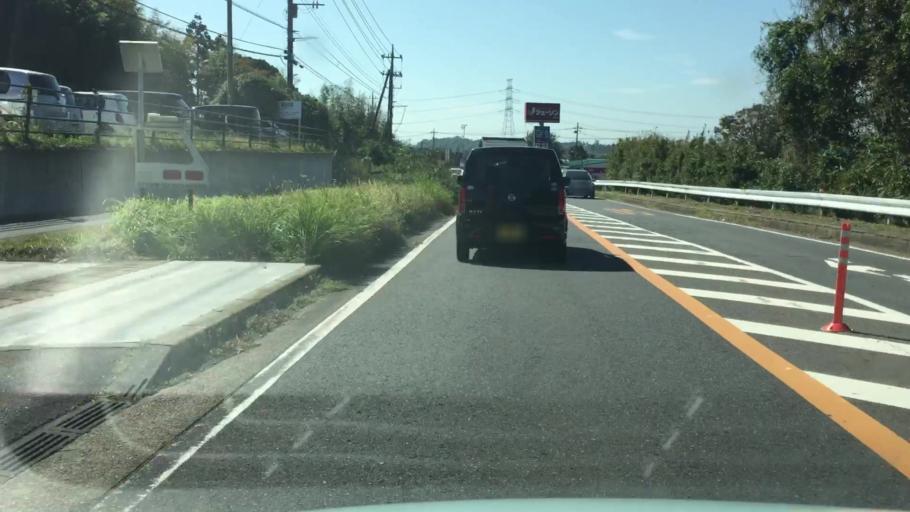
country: JP
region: Ibaraki
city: Ryugasaki
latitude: 35.8754
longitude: 140.1558
